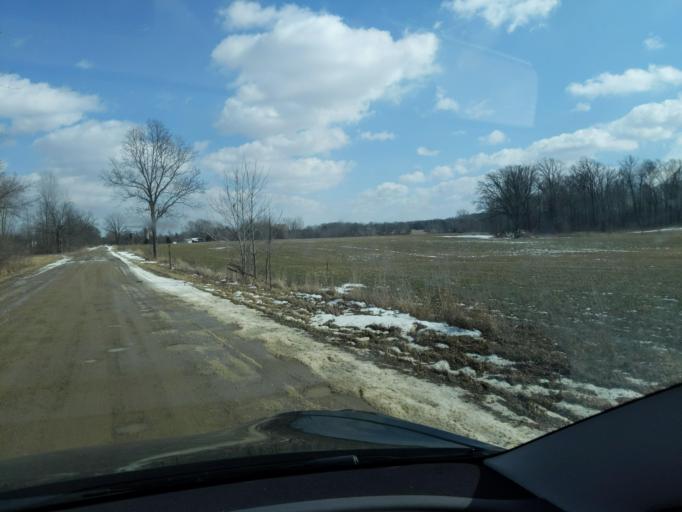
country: US
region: Michigan
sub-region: Ingham County
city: Webberville
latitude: 42.6138
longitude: -84.1413
